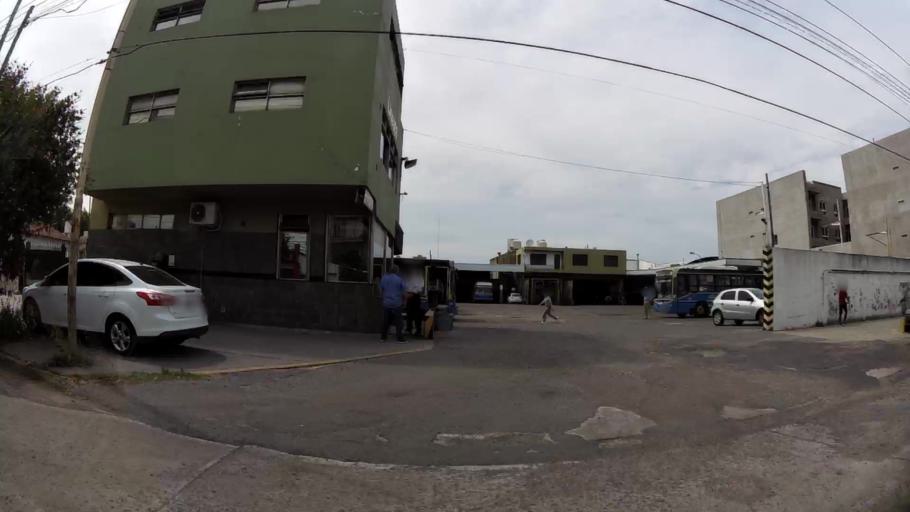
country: AR
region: Buenos Aires F.D.
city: Villa Lugano
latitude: -34.6899
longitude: -58.4978
